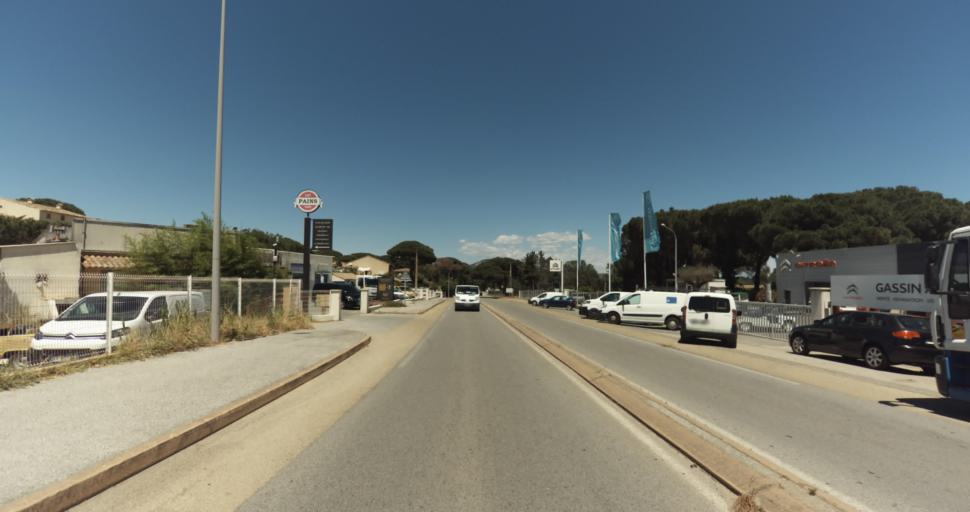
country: FR
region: Provence-Alpes-Cote d'Azur
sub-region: Departement du Var
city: Gassin
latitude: 43.2505
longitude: 6.5731
